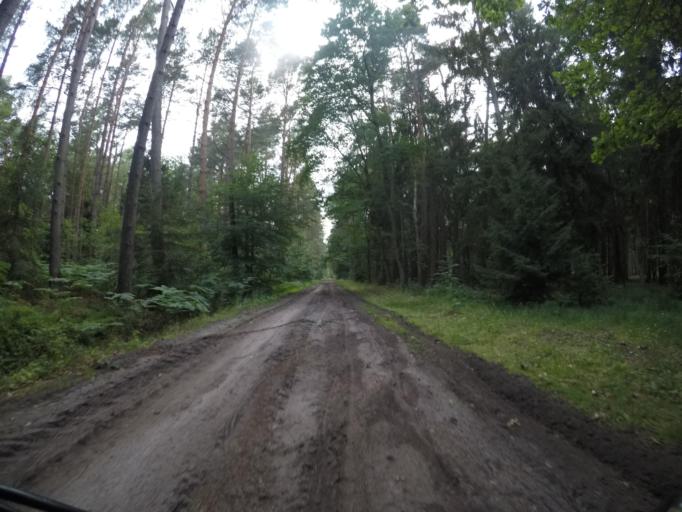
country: DE
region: Mecklenburg-Vorpommern
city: Lubtheen
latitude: 53.2501
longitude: 11.0224
